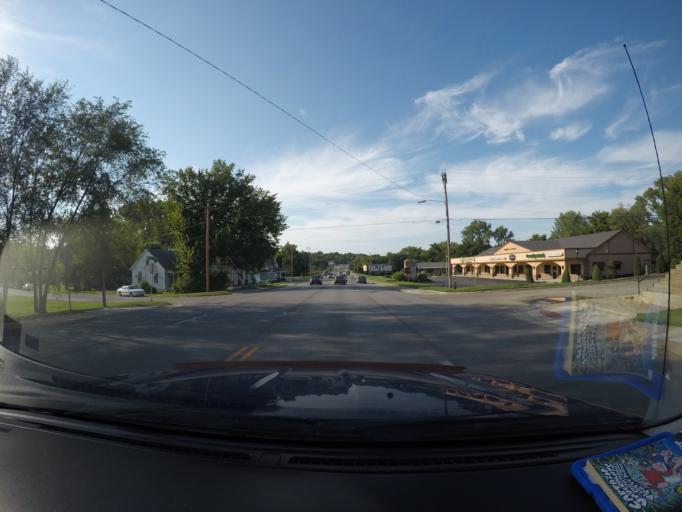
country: US
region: Kansas
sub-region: Leavenworth County
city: Leavenworth
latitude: 39.2913
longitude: -94.9077
